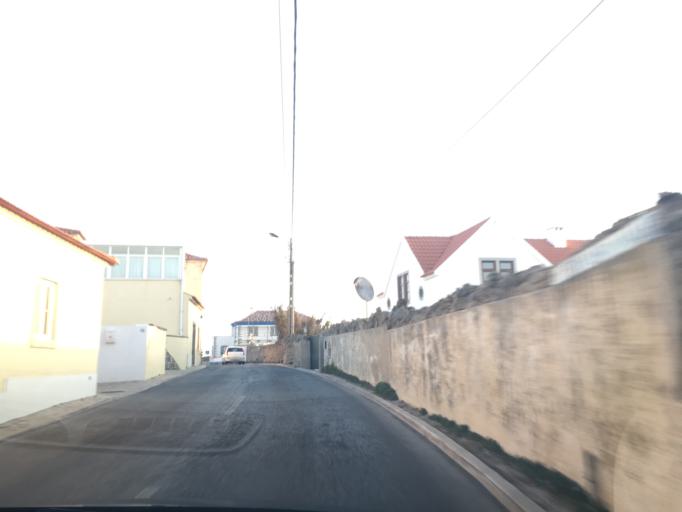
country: PT
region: Lisbon
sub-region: Sintra
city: Colares
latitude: 38.8372
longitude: -9.4644
